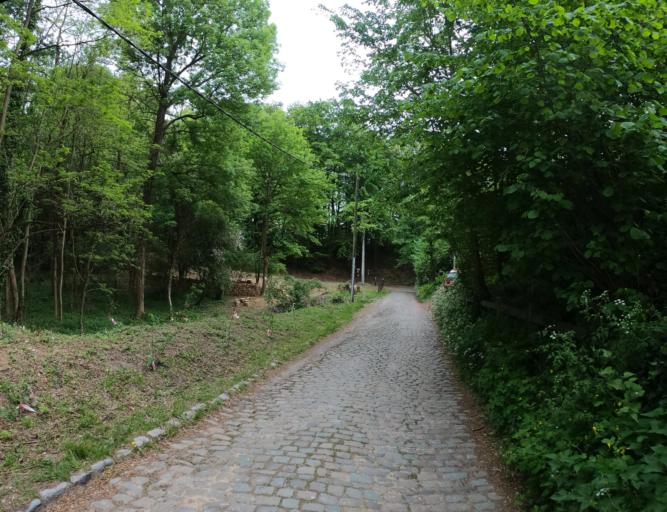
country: BE
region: Flanders
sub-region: Provincie Vlaams-Brabant
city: Beersel
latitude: 50.7361
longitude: 4.3080
